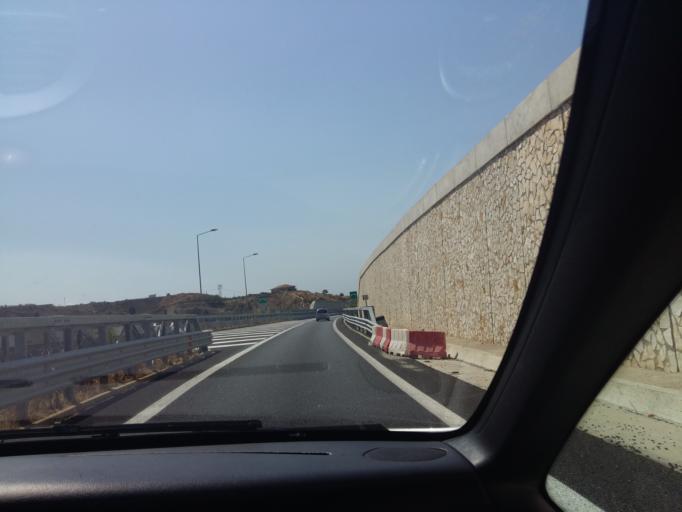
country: IT
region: Calabria
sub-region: Provincia di Reggio Calabria
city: Campo Calabro
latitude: 38.2146
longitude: 15.6471
